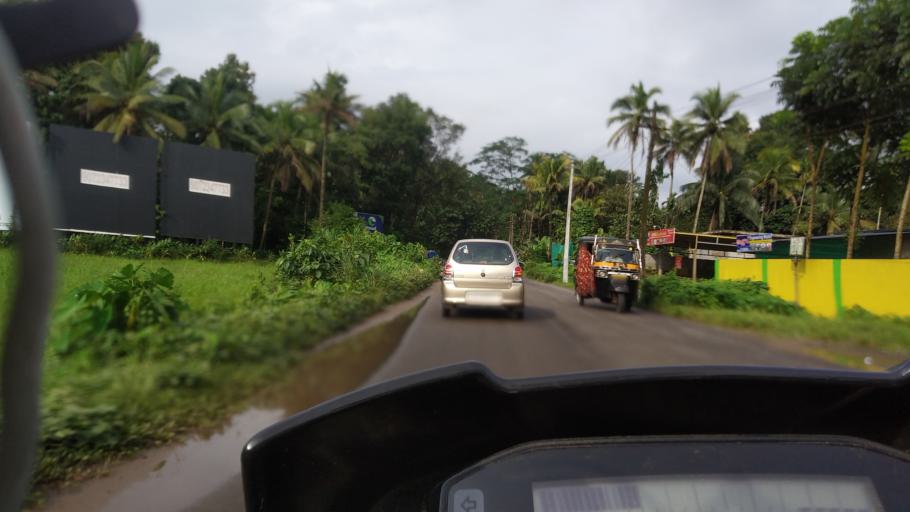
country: IN
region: Kerala
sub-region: Ernakulam
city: Kotamangalam
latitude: 10.0493
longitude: 76.7217
